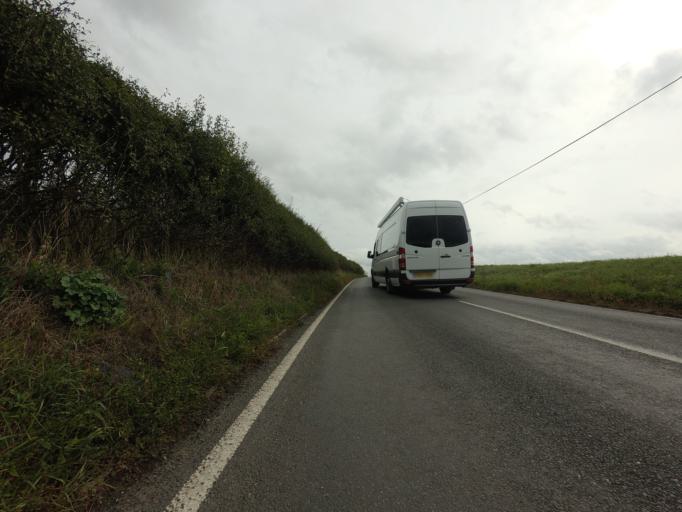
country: GB
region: England
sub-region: Cambridgeshire
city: Duxford
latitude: 52.0208
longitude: 0.1407
